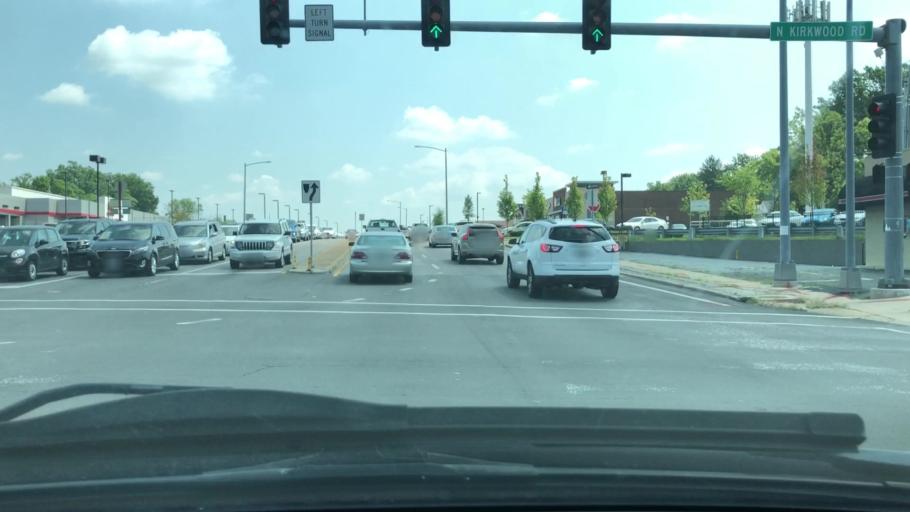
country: US
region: Missouri
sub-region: Saint Louis County
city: Kirkwood
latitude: 38.6001
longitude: -90.4064
